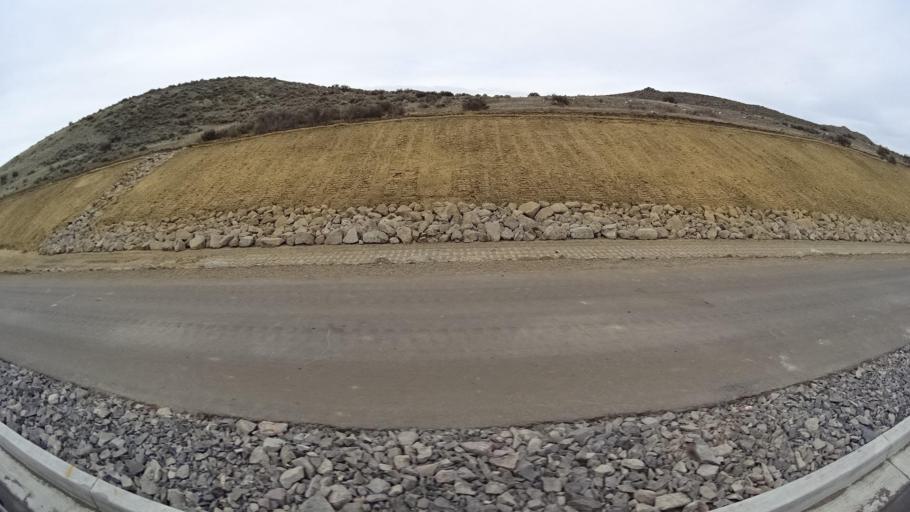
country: US
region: Nevada
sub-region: Washoe County
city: Lemmon Valley
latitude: 39.6183
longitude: -119.8486
